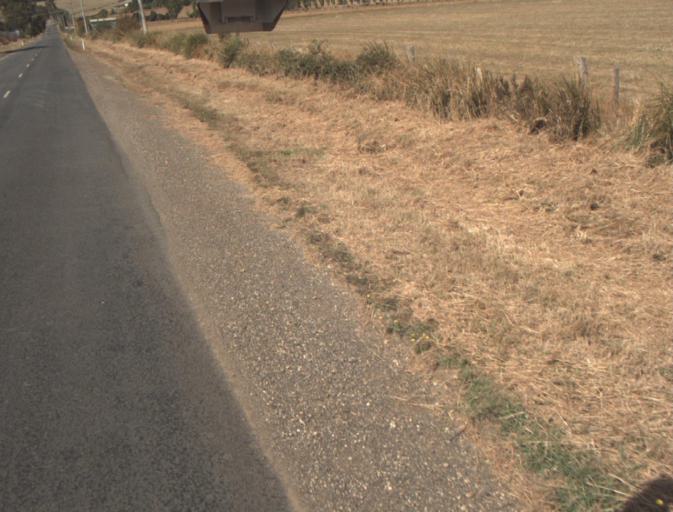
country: AU
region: Tasmania
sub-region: Launceston
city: Mayfield
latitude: -41.2501
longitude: 147.1479
